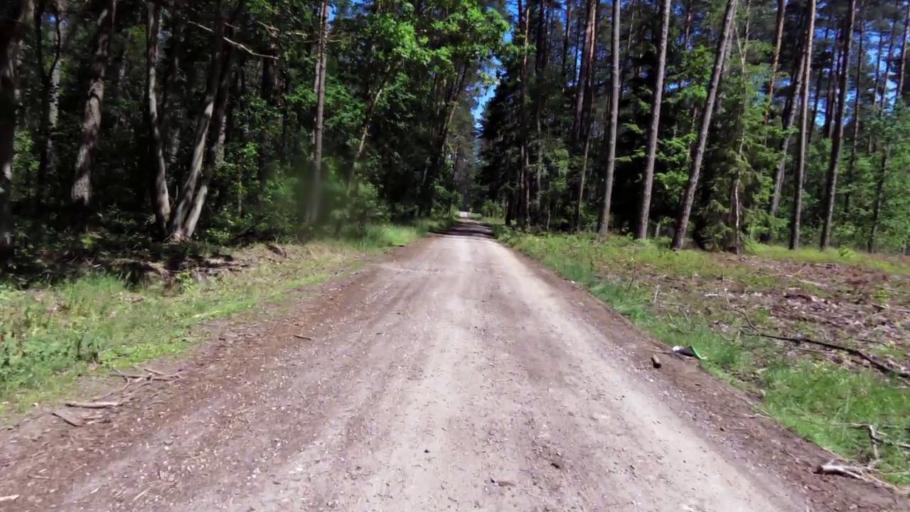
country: PL
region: West Pomeranian Voivodeship
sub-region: Powiat bialogardzki
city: Tychowo
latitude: 53.9343
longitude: 16.1236
